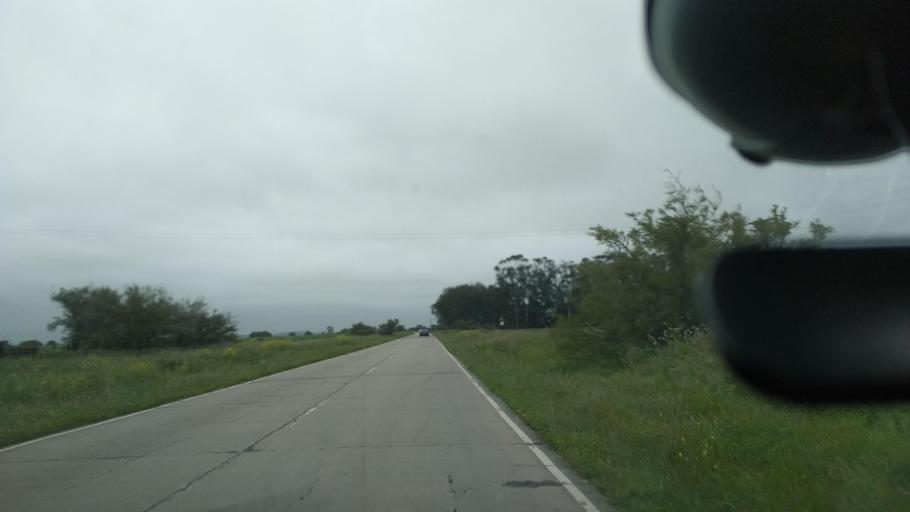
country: AR
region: Buenos Aires
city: Veronica
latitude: -35.5794
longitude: -57.2777
